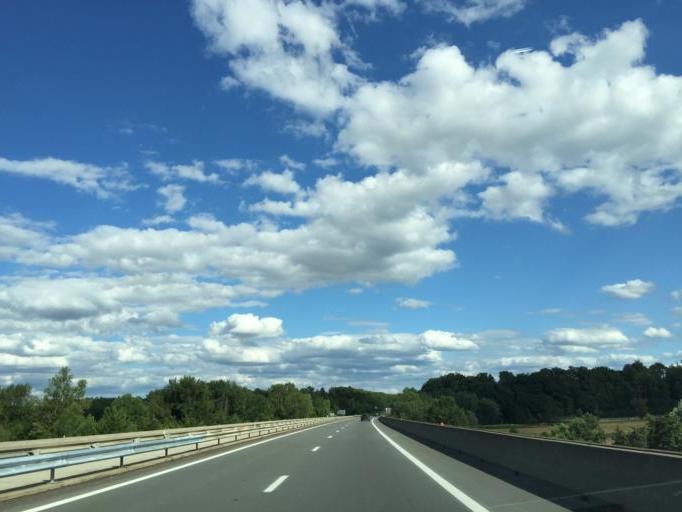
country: FR
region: Rhone-Alpes
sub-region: Departement de la Loire
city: Andrezieux-Boutheon
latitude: 45.5529
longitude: 4.2626
